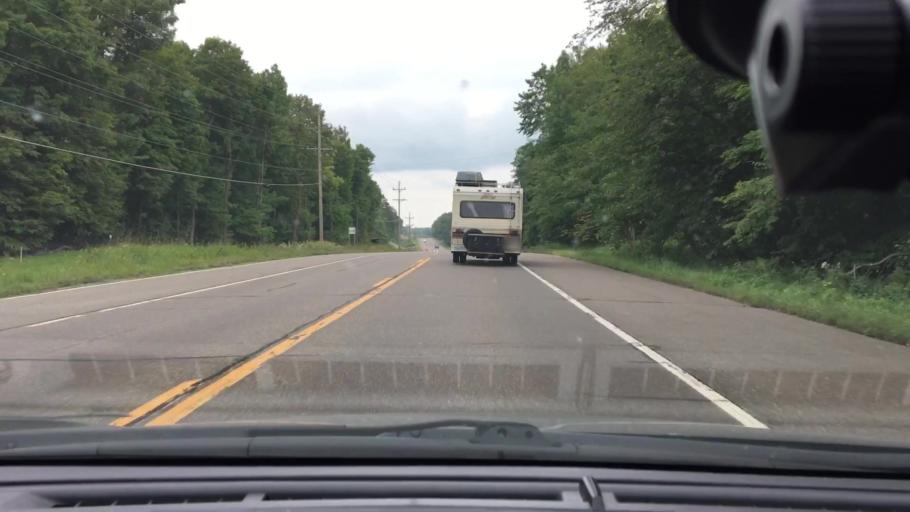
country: US
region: Minnesota
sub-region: Crow Wing County
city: Crosby
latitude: 46.4898
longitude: -93.9119
